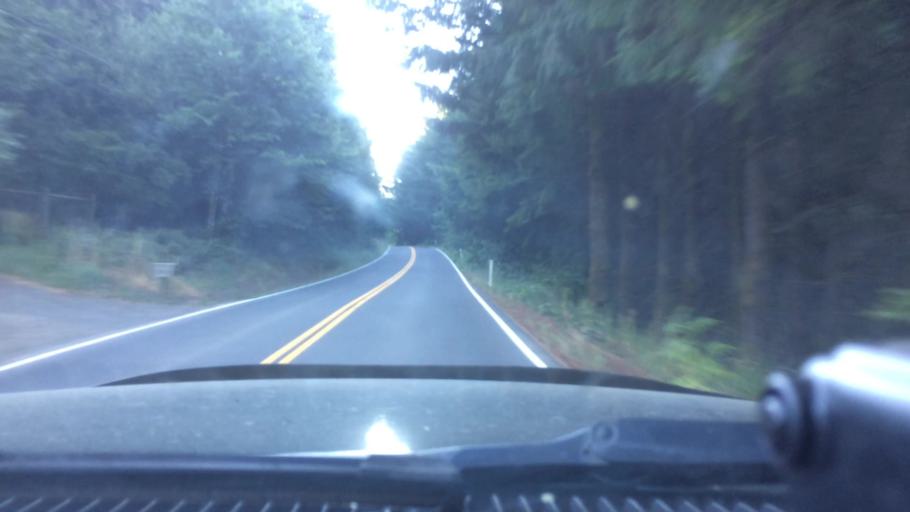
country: US
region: Oregon
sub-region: Yamhill County
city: Newberg
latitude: 45.3445
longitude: -122.9595
